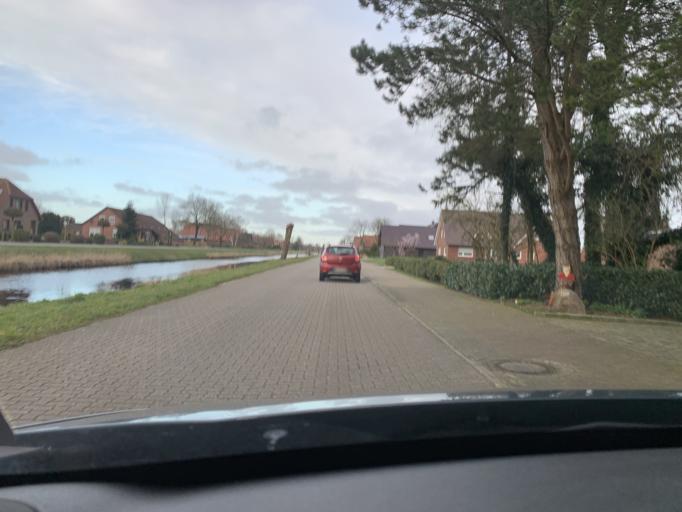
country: DE
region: Lower Saxony
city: Schwerinsdorf
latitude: 53.2749
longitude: 7.7024
